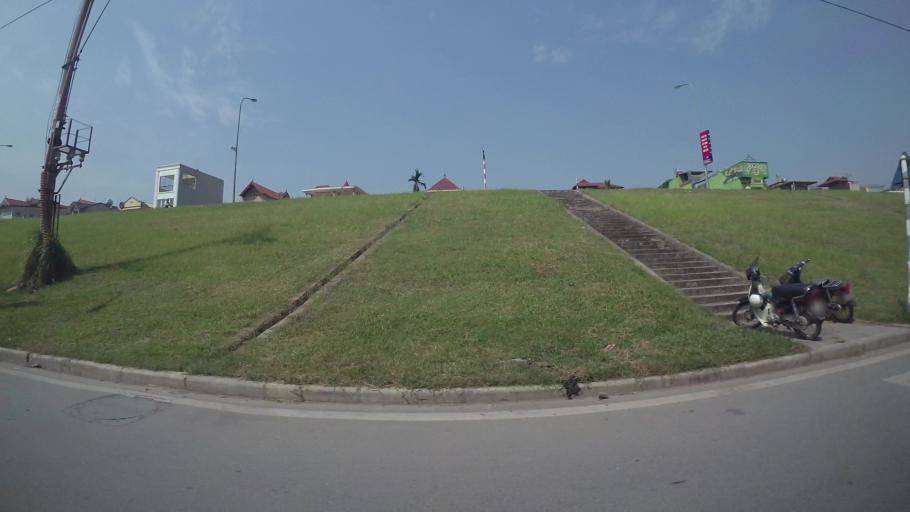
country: VN
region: Ha Noi
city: Hoan Kiem
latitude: 21.0591
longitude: 105.8645
